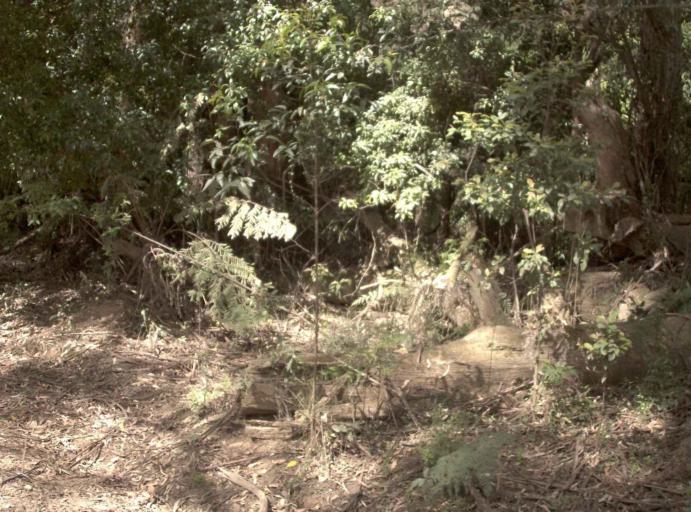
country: AU
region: Victoria
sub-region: East Gippsland
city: Lakes Entrance
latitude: -37.5834
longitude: 148.7265
